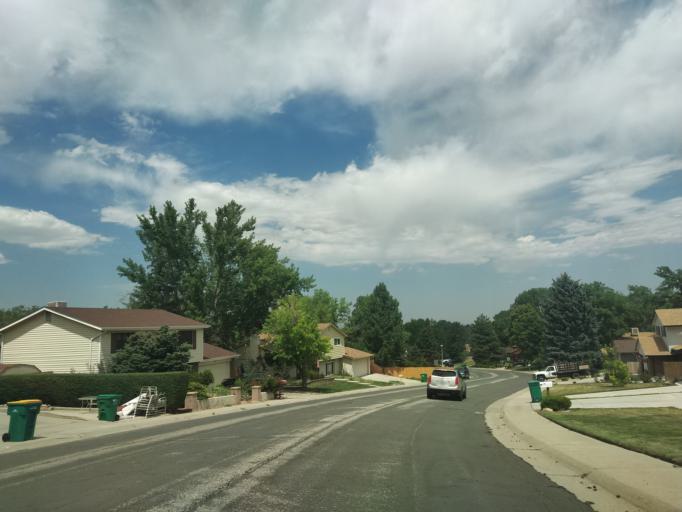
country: US
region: Colorado
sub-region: Jefferson County
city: Lakewood
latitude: 39.6864
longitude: -105.1244
